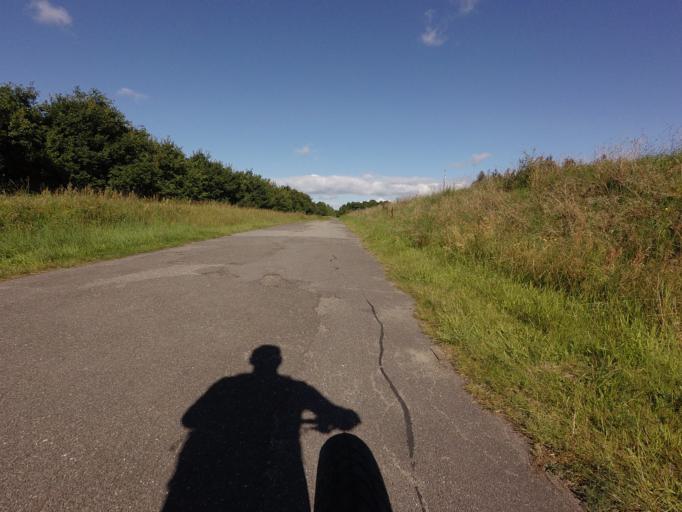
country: DK
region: Central Jutland
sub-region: Horsens Kommune
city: Horsens
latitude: 55.9603
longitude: 9.7671
